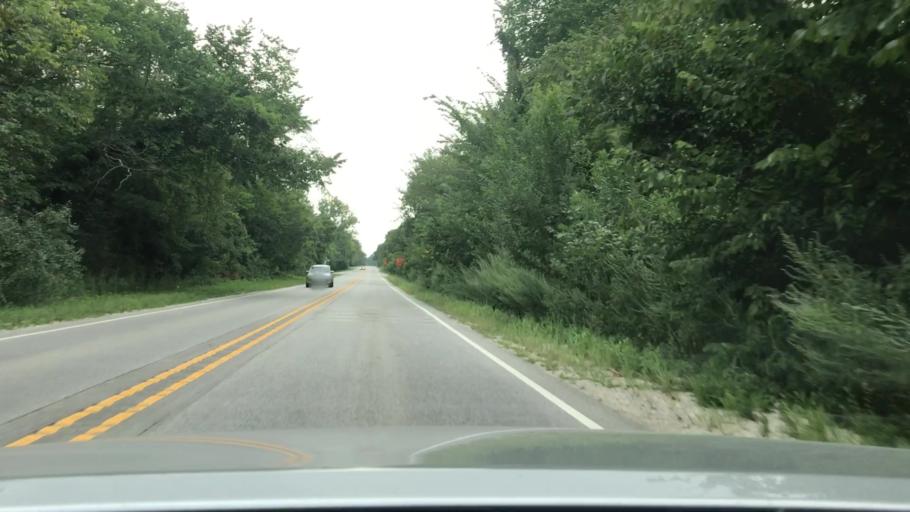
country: US
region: Illinois
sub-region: Will County
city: Goodings Grove
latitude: 41.6875
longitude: -87.9171
